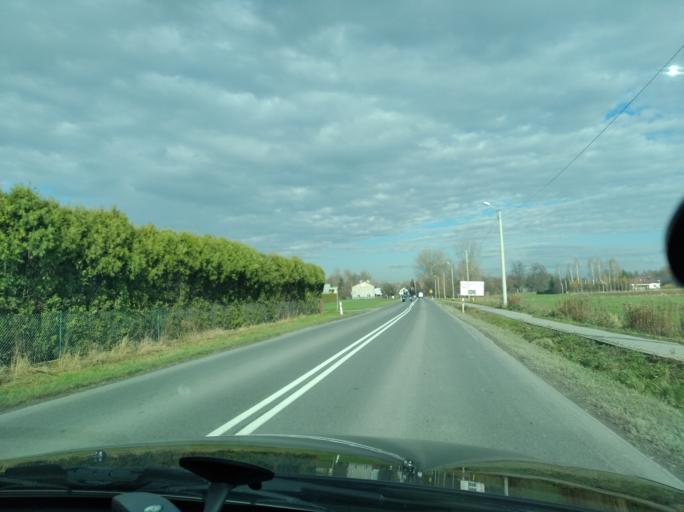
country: PL
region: Subcarpathian Voivodeship
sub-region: Powiat ropczycko-sedziszowski
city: Ostrow
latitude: 50.0928
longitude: 21.5929
